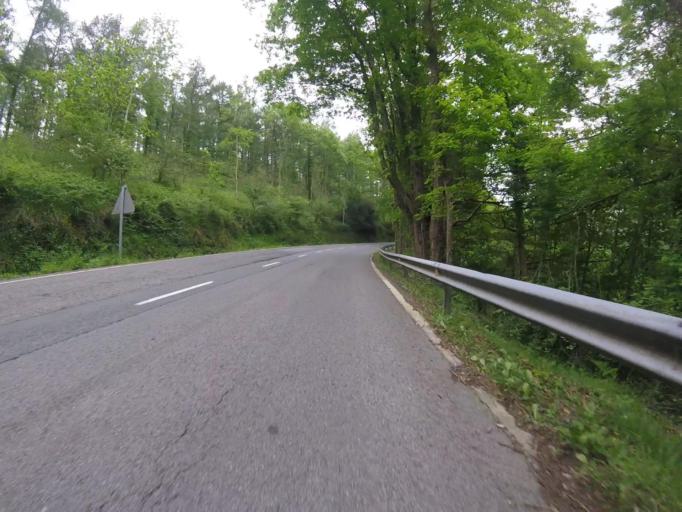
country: ES
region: Navarre
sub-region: Provincia de Navarra
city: Zugarramurdi
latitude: 43.2623
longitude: -1.4890
